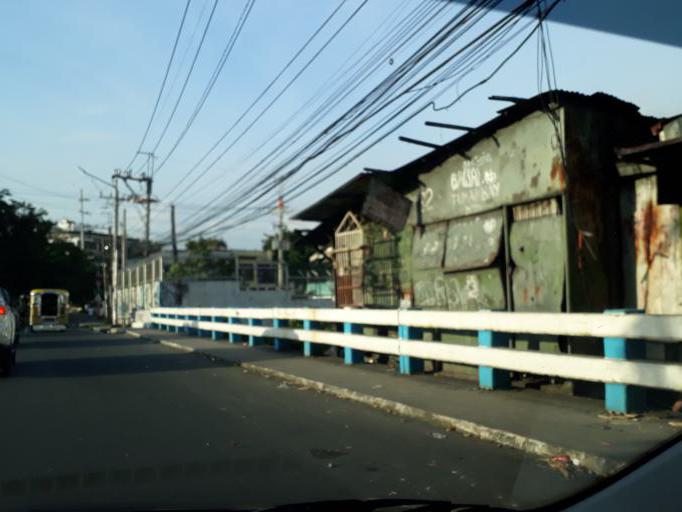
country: PH
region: Calabarzon
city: Bagong Pagasa
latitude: 14.6613
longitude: 121.0202
